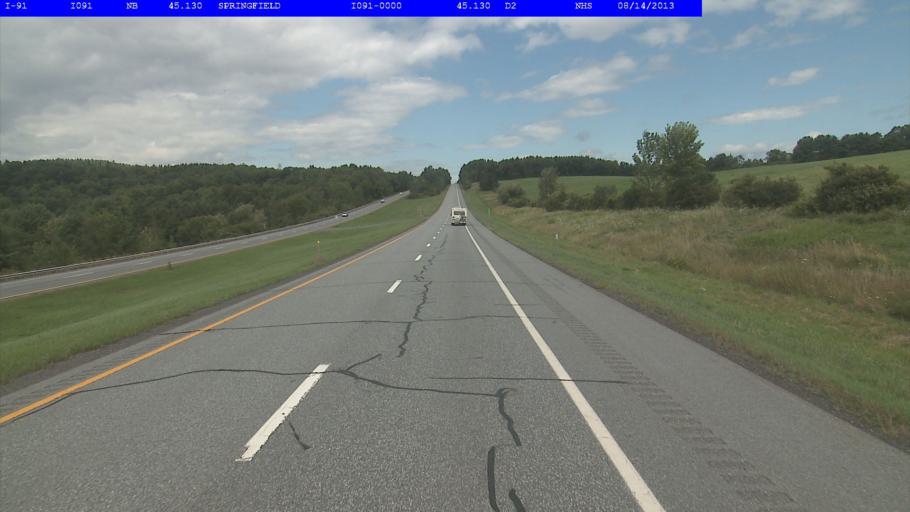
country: US
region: Vermont
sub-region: Windsor County
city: Springfield
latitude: 43.3144
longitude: -72.4210
